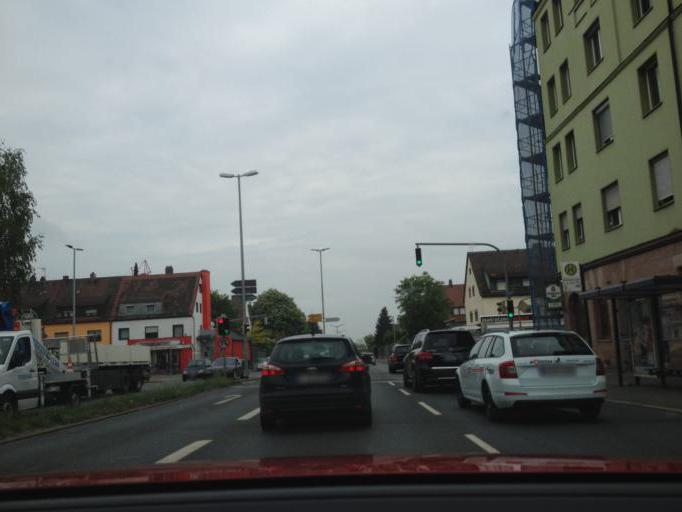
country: DE
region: Bavaria
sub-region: Regierungsbezirk Mittelfranken
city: Grossreuth bei Schweinau
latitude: 49.4404
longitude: 11.0361
